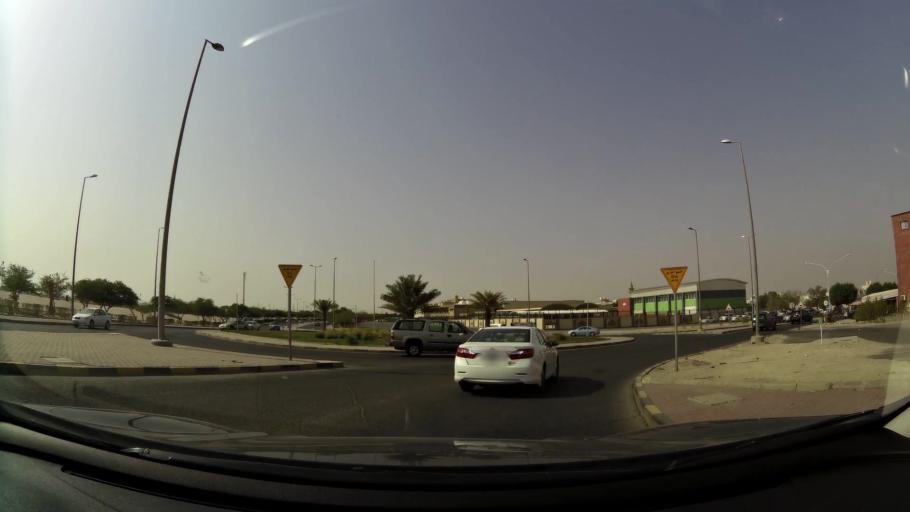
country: KW
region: Muhafazat al Jahra'
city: Al Jahra'
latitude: 29.3215
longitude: 47.6537
